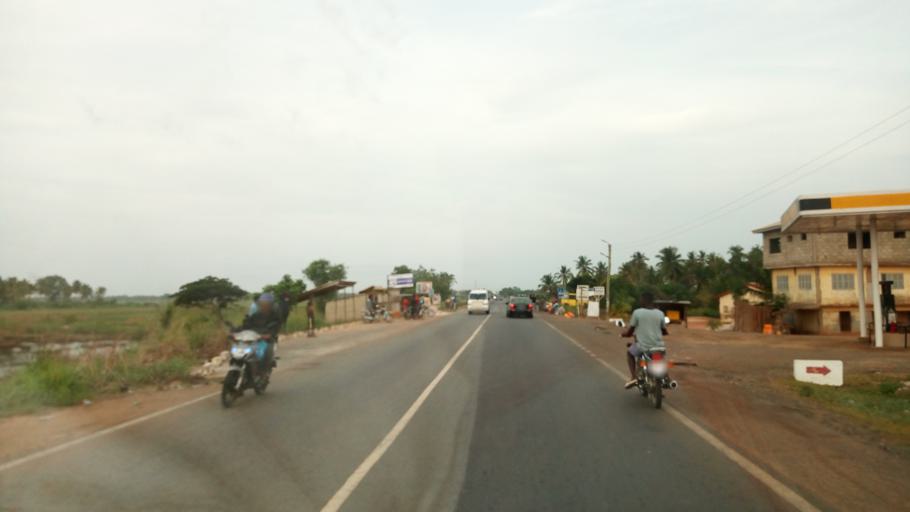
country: GH
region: Volta
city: Keta
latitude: 6.0714
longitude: 1.0288
